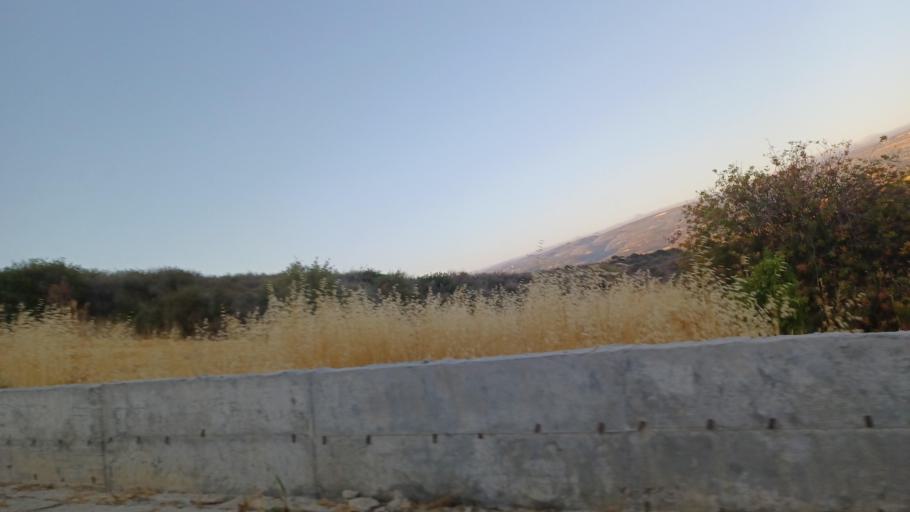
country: CY
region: Pafos
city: Polis
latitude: 34.9954
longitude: 32.4699
